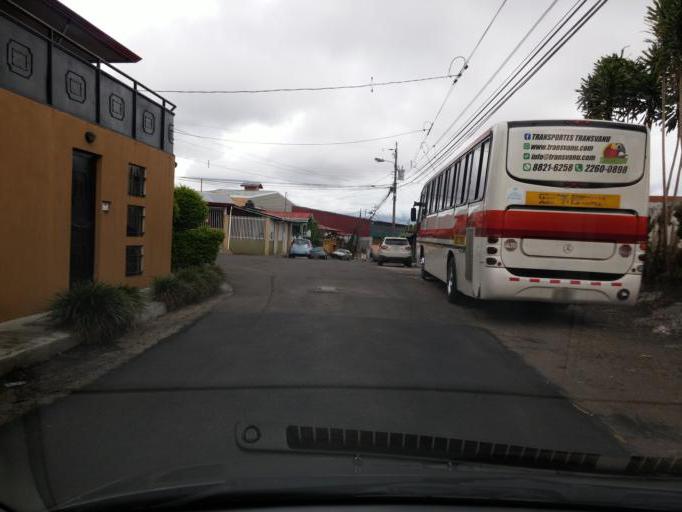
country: CR
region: Heredia
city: Mercedes
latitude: 10.0318
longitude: -84.1354
